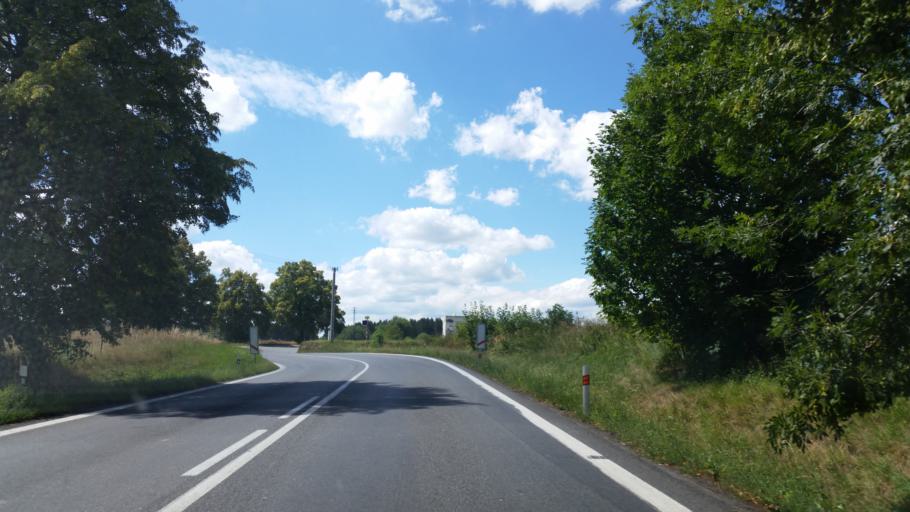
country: CZ
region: Vysocina
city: Cernovice
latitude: 49.4267
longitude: 14.9317
